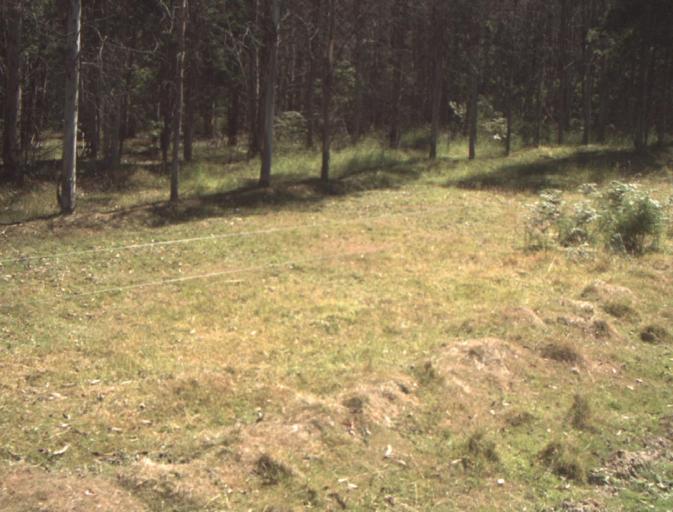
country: AU
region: Tasmania
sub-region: Dorset
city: Scottsdale
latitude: -41.2728
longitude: 147.3479
